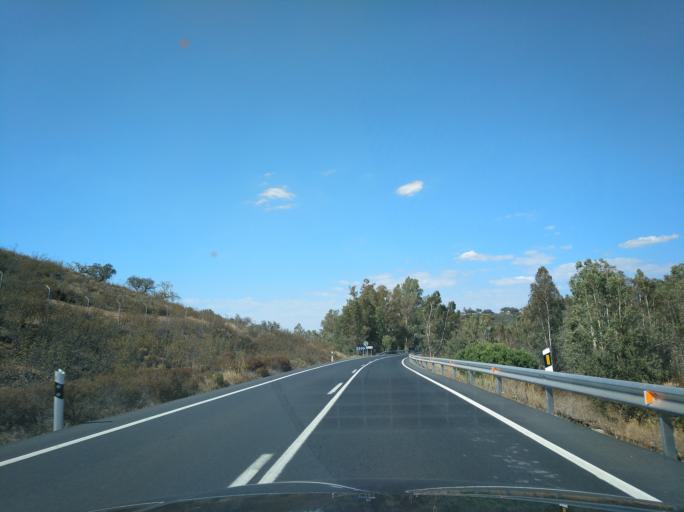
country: ES
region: Andalusia
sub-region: Provincia de Huelva
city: Alosno
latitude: 37.5269
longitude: -7.1343
